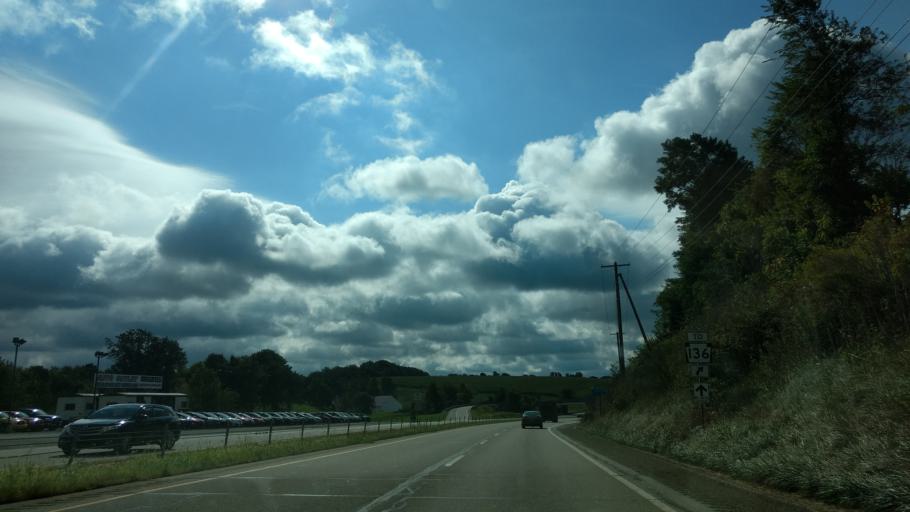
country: US
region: Pennsylvania
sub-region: Westmoreland County
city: Fellsburg
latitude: 40.2191
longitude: -79.8452
